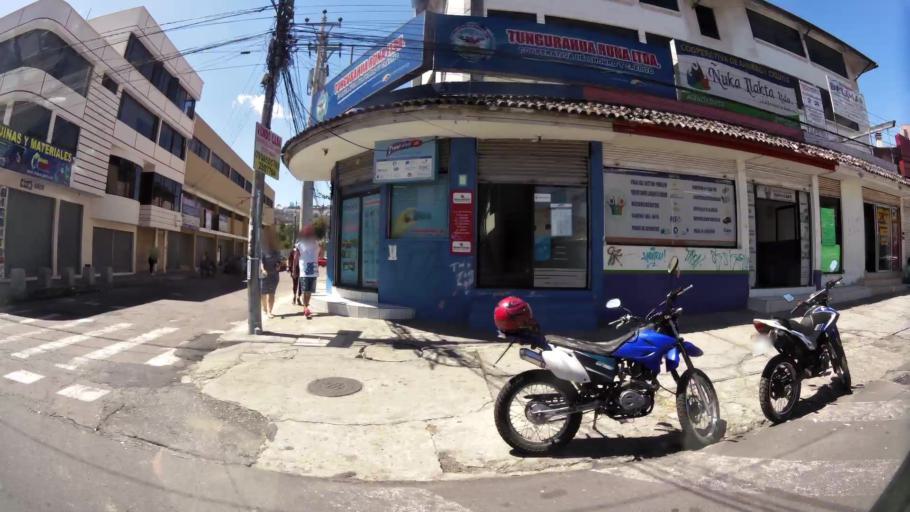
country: EC
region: Pichincha
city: Quito
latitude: -0.1174
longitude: -78.4911
